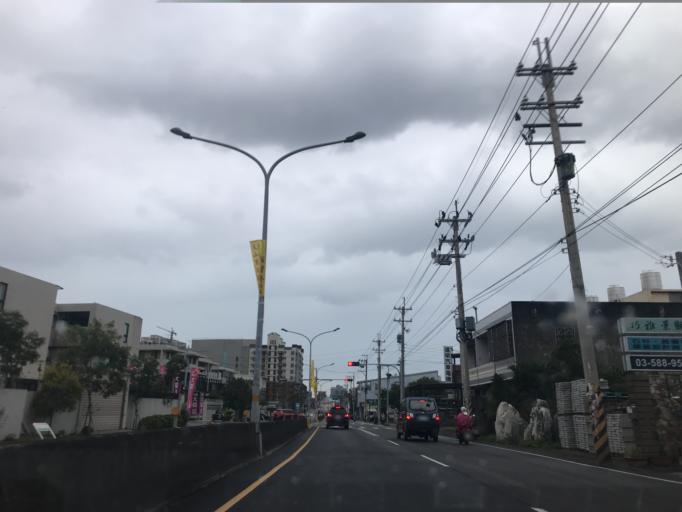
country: TW
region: Taiwan
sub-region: Hsinchu
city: Zhubei
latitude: 24.8318
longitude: 121.0317
